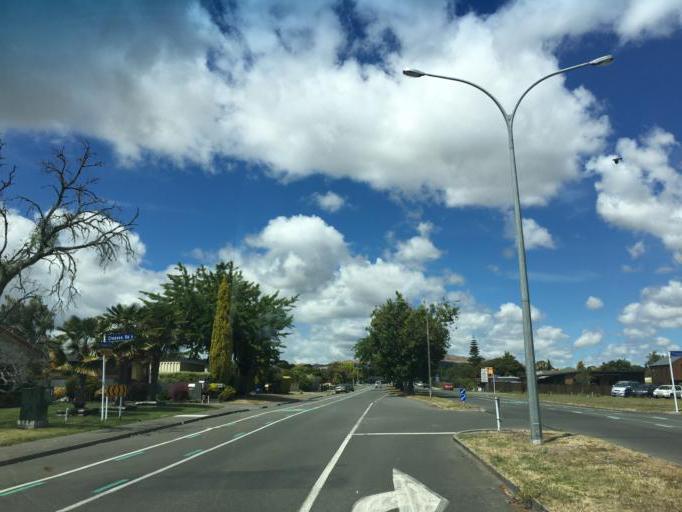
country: NZ
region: Hawke's Bay
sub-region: Hastings District
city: Hastings
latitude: -39.6621
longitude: 176.8840
